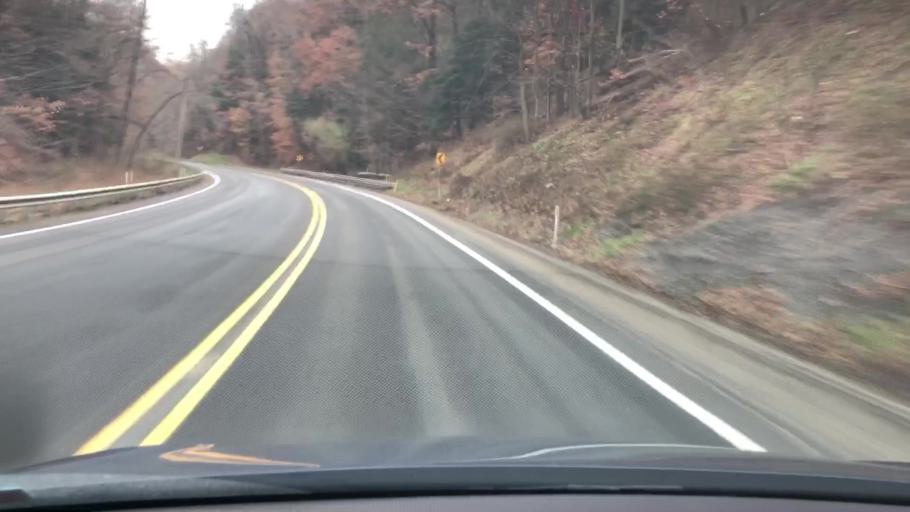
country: US
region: Pennsylvania
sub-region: Armstrong County
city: Kittanning
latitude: 40.9612
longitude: -79.3647
